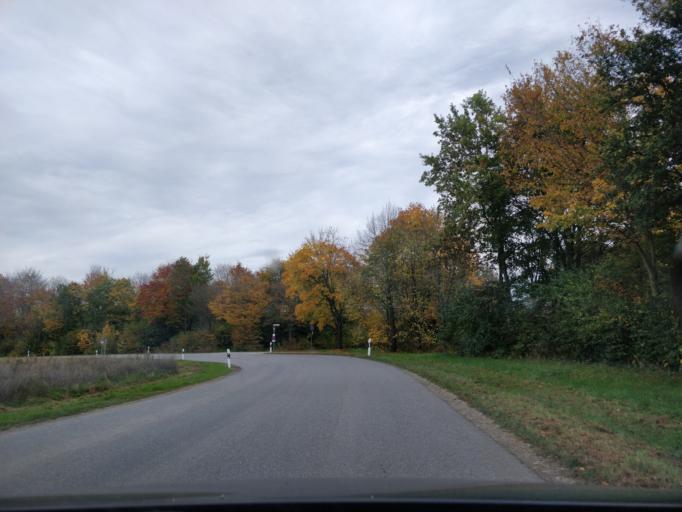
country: DE
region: Bavaria
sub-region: Swabia
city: Mering
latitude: 48.2700
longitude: 10.9712
